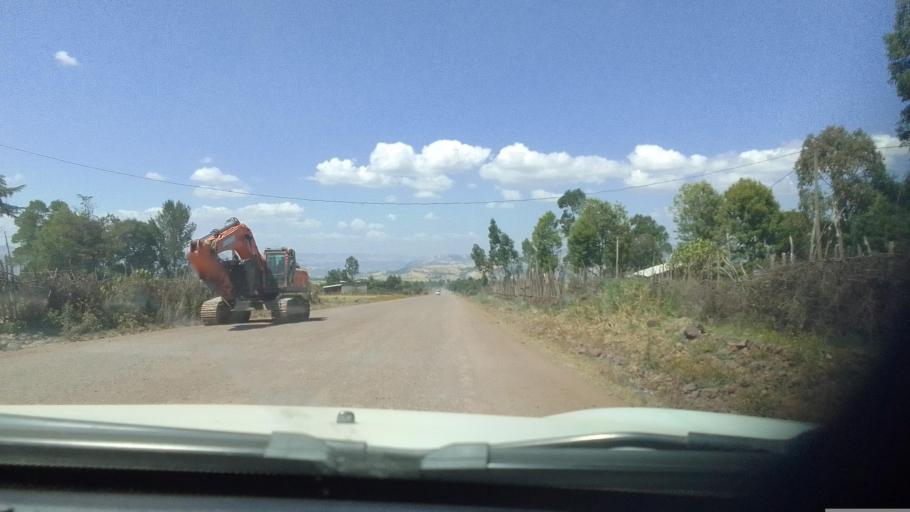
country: ET
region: Oromiya
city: Hagere Hiywet
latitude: 8.9250
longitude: 37.8627
